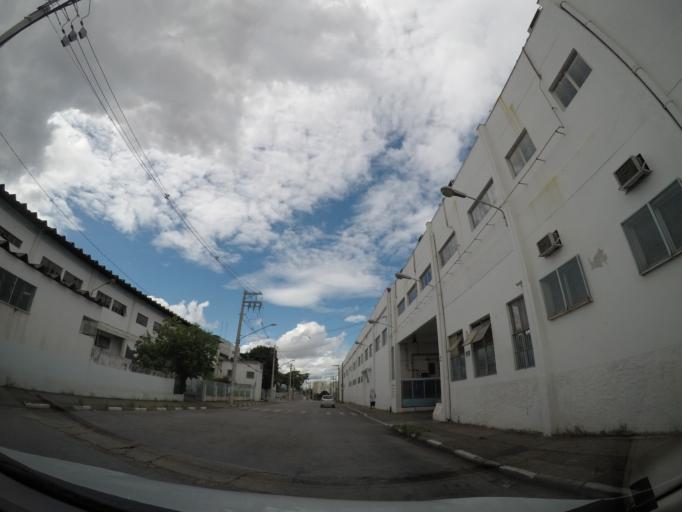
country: BR
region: Sao Paulo
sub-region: Guarulhos
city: Guarulhos
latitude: -23.4937
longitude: -46.5569
